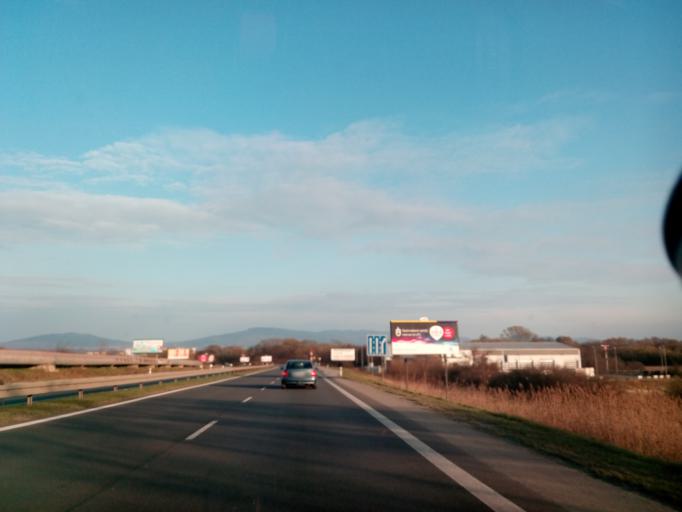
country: SK
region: Kosicky
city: Kosice
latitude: 48.6900
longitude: 21.2450
